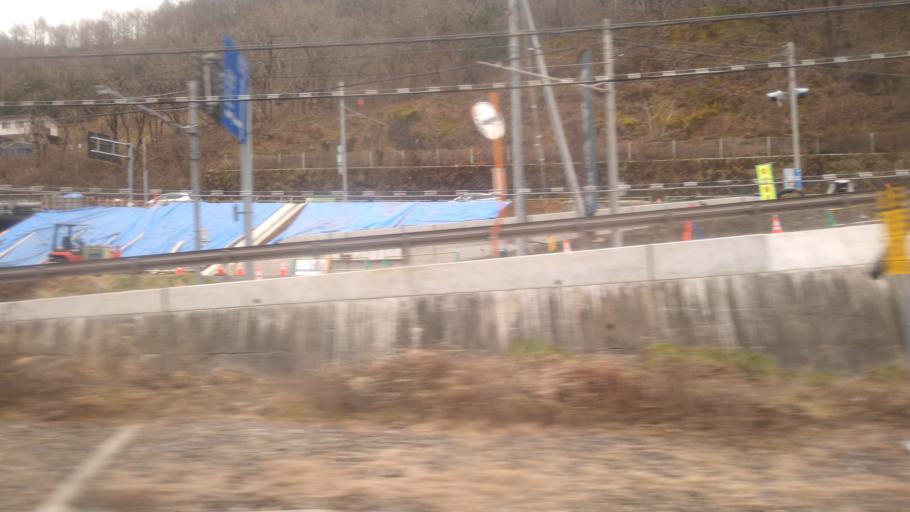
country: JP
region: Nagano
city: Ina
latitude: 35.9278
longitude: 137.7837
